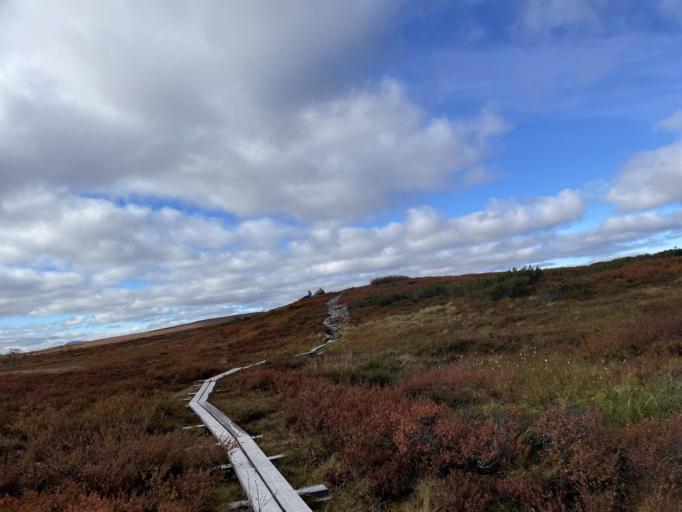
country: SE
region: Jaemtland
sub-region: Are Kommun
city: Are
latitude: 62.6949
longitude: 12.9261
